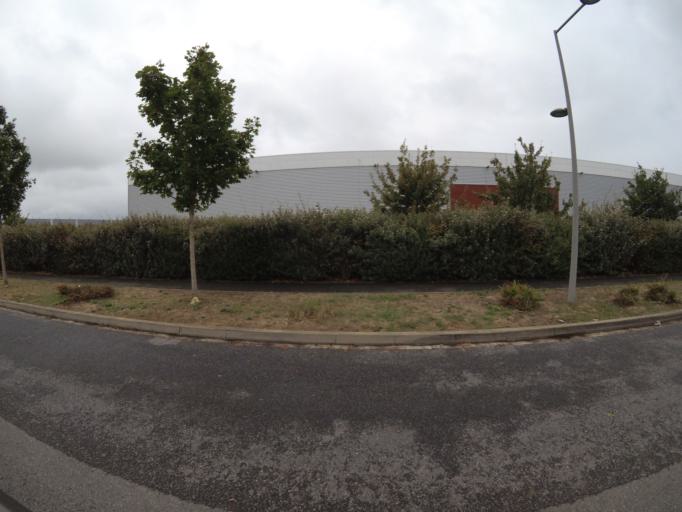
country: FR
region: Ile-de-France
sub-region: Departement de Seine-et-Marne
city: Montevrain
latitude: 48.8617
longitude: 2.7510
